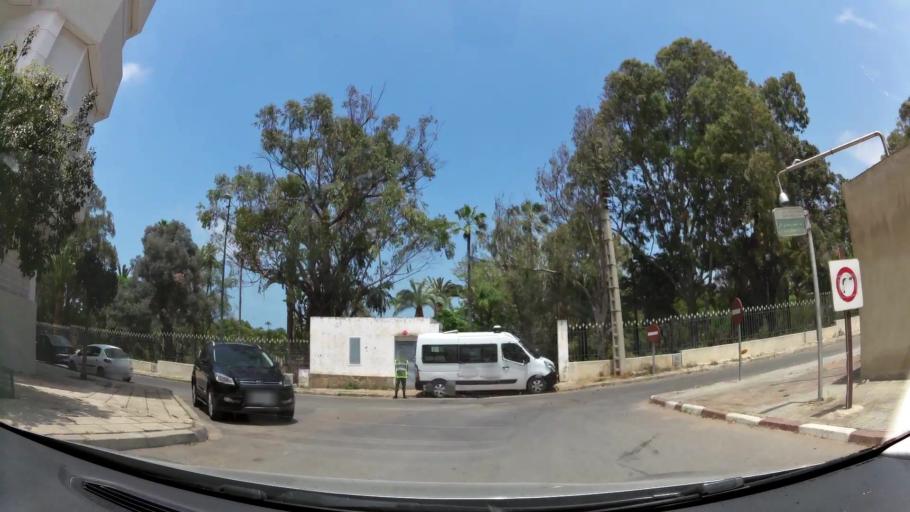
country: MA
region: Rabat-Sale-Zemmour-Zaer
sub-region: Rabat
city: Rabat
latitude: 34.0076
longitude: -6.8473
